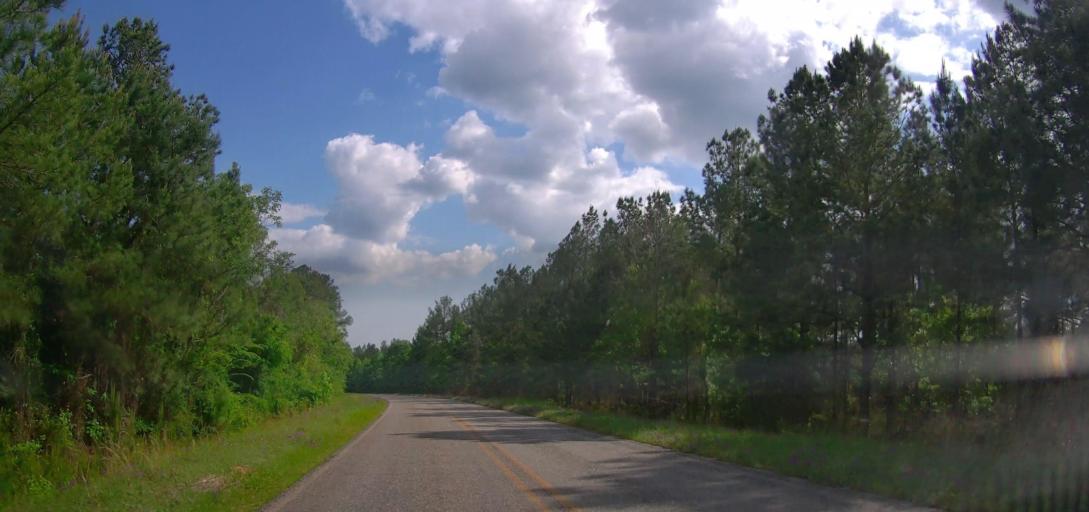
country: US
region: Georgia
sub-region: Laurens County
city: East Dublin
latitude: 32.7072
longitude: -82.9183
